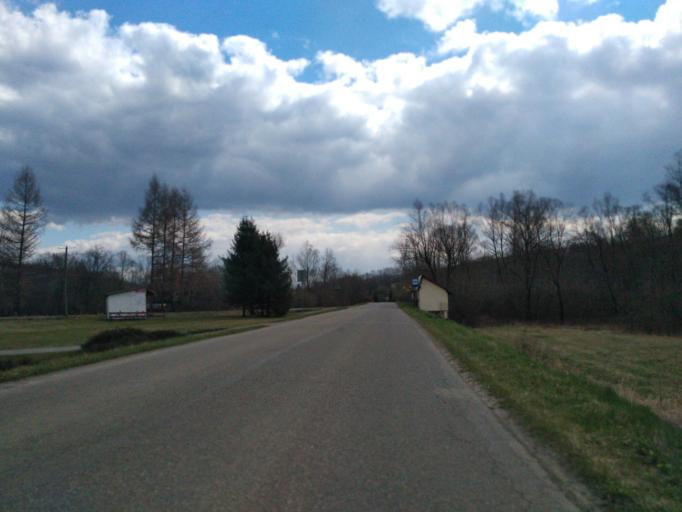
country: PL
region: Subcarpathian Voivodeship
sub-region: Powiat sanocki
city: Tyrawa Woloska
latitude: 49.6014
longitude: 22.3140
